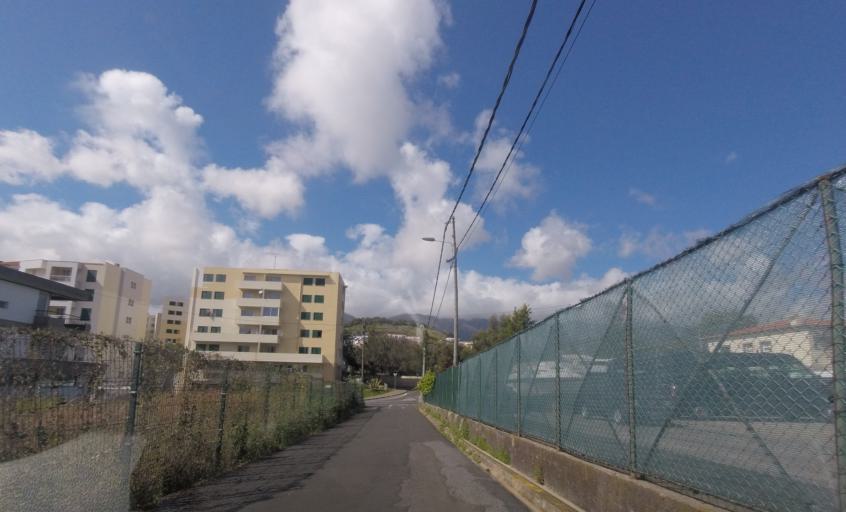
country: PT
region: Madeira
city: Camara de Lobos
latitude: 32.6447
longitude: -16.9398
